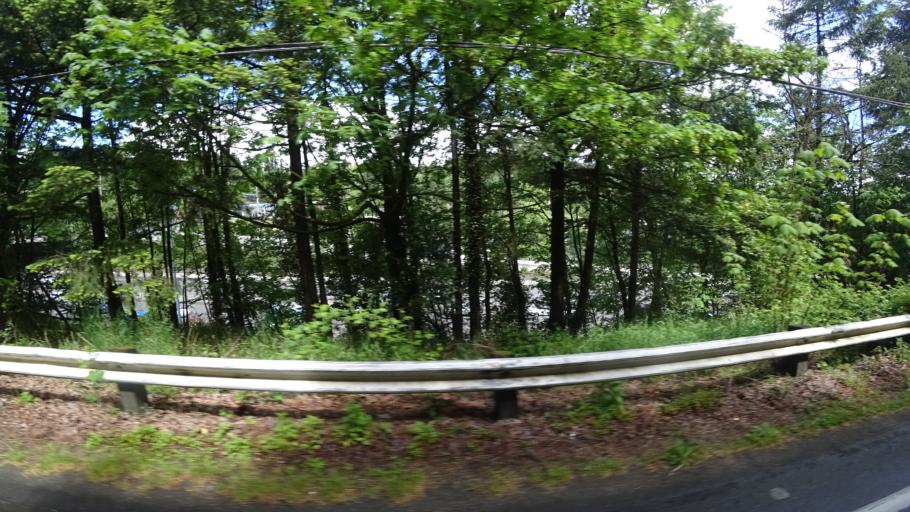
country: US
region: Oregon
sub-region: Washington County
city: West Slope
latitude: 45.5082
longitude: -122.7340
